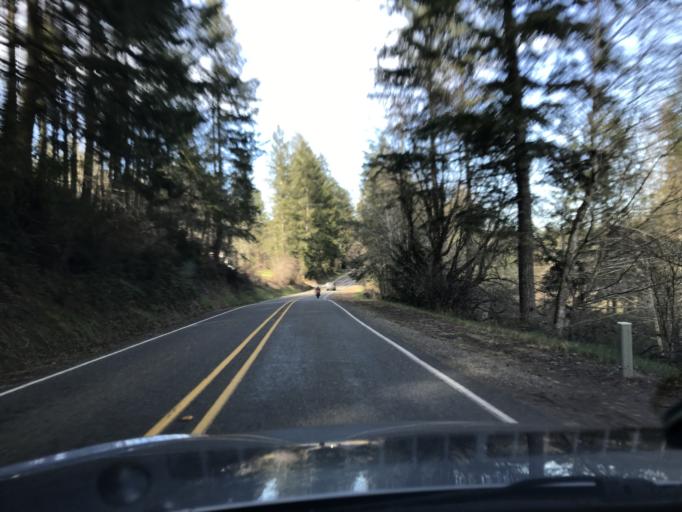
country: US
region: Washington
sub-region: Pierce County
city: Longbranch
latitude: 47.2348
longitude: -122.7890
